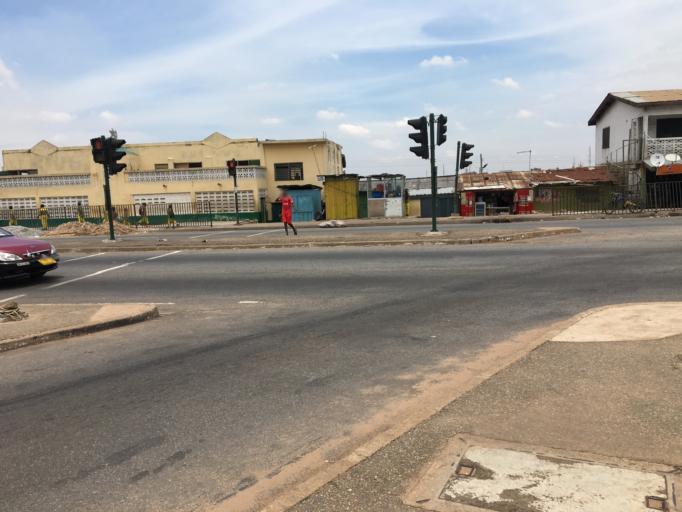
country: GH
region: Greater Accra
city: Accra
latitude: 5.5876
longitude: -0.1923
